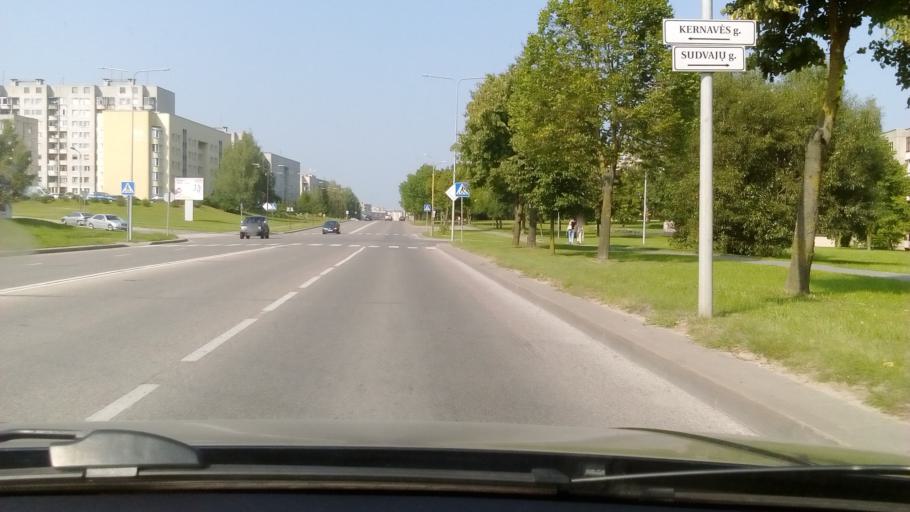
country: LT
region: Alytaus apskritis
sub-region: Alytus
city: Alytus
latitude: 54.3884
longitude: 24.0252
